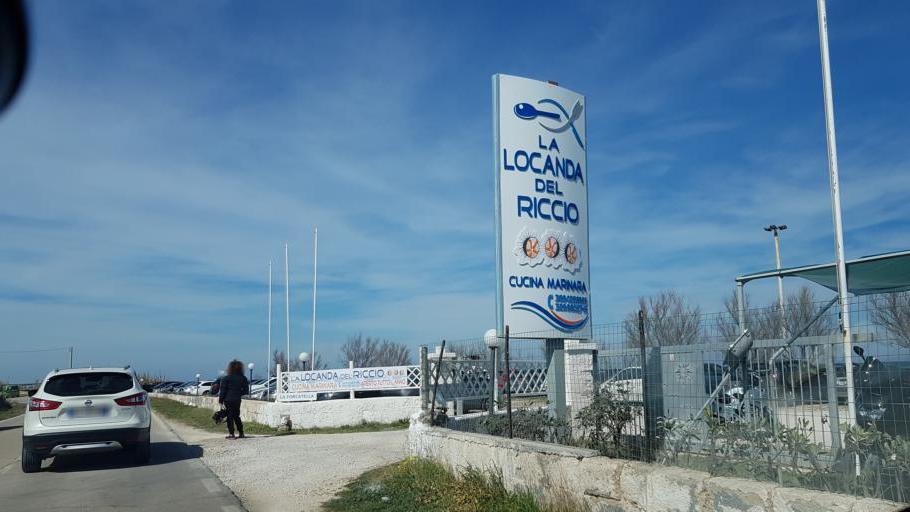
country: IT
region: Apulia
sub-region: Provincia di Brindisi
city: Pezze di Greco
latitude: 40.8557
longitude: 17.4410
